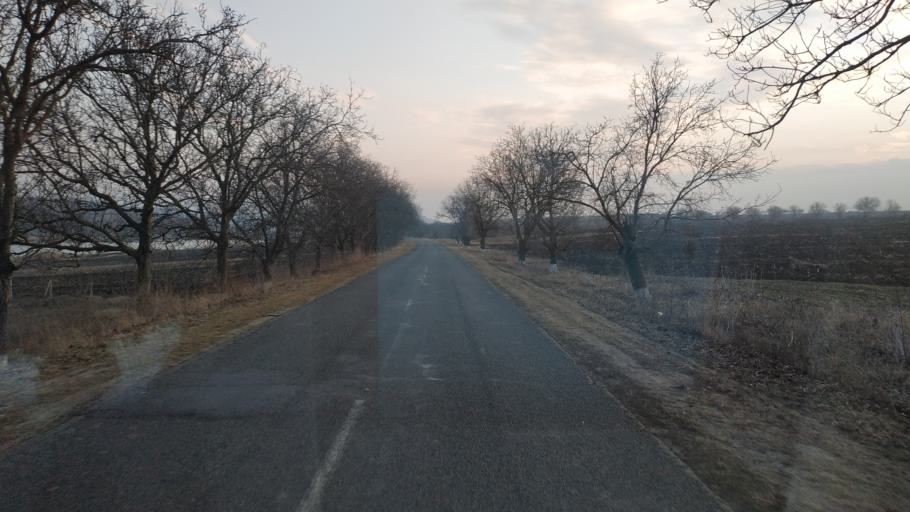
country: MD
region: Hincesti
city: Dancu
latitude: 46.7010
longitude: 28.3378
